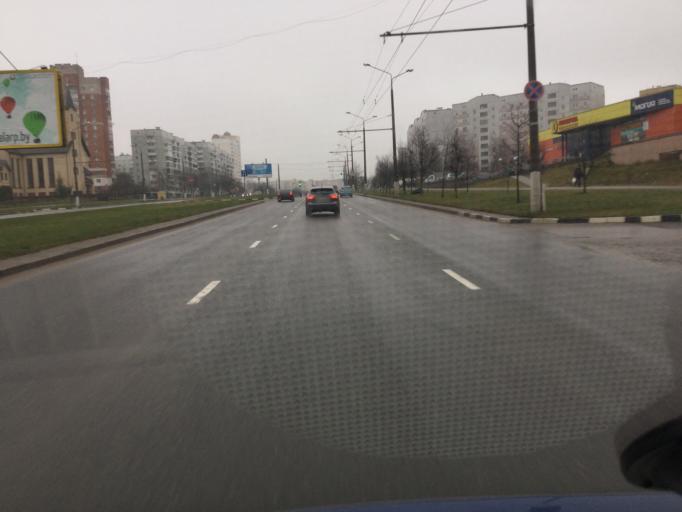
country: BY
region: Vitebsk
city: Vitebsk
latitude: 55.1631
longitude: 30.2126
